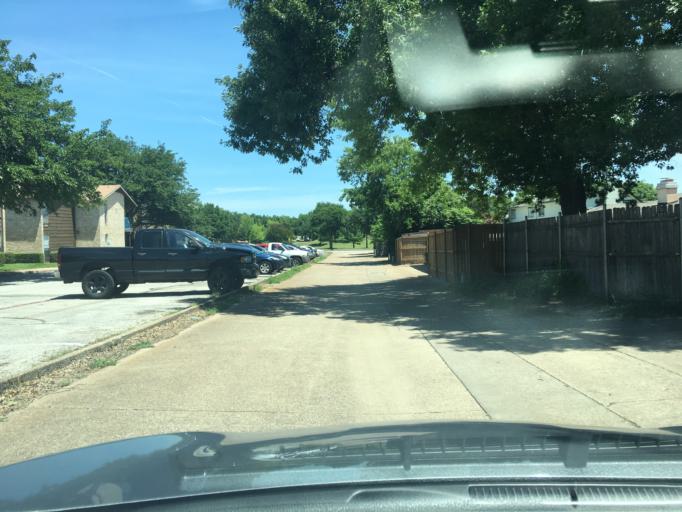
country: US
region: Texas
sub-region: Dallas County
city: Richardson
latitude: 32.9469
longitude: -96.6961
